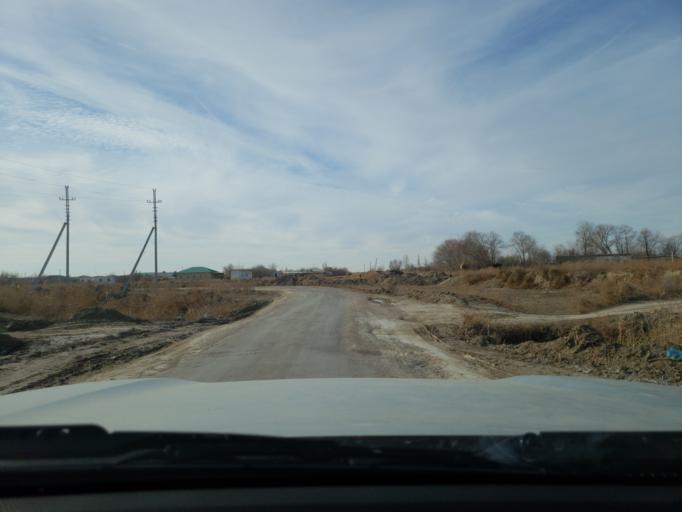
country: TM
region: Dasoguz
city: Dasoguz
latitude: 41.8492
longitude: 59.8820
